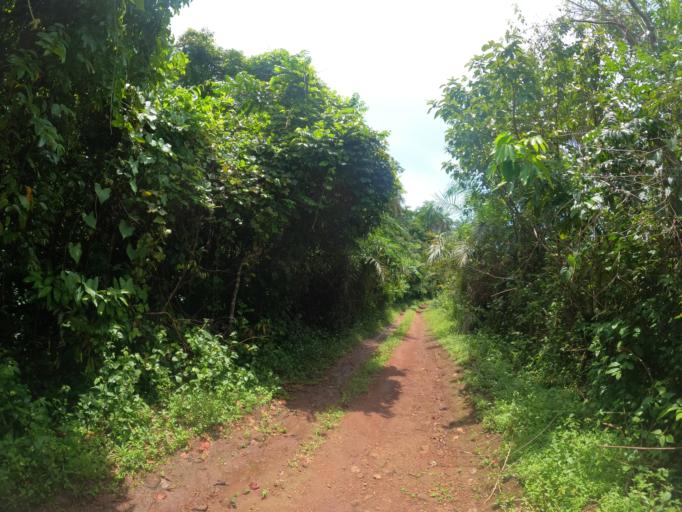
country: SL
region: Northern Province
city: Binkolo
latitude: 9.1579
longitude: -12.1914
